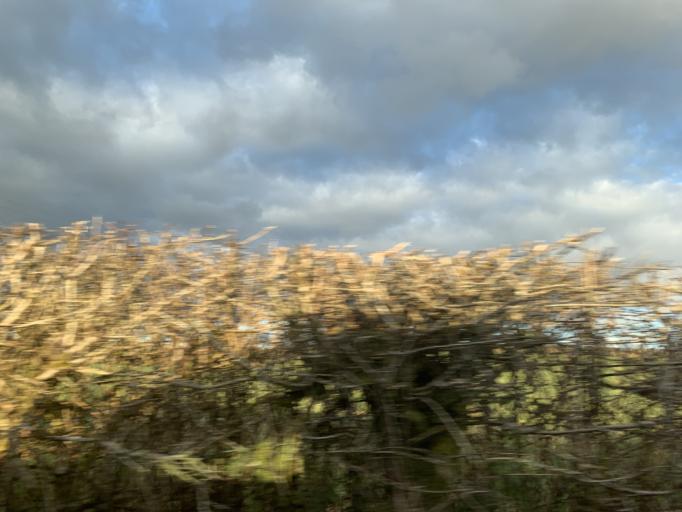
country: IE
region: Connaught
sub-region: Maigh Eo
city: Ballyhaunis
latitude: 53.8231
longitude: -8.7003
